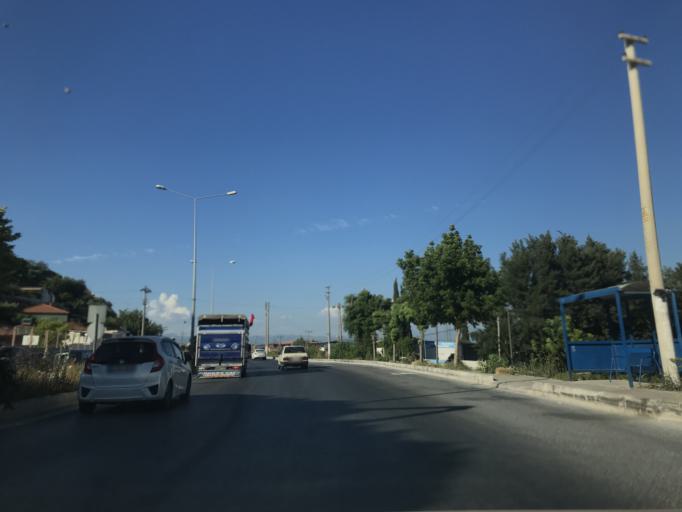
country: TR
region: Aydin
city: Soeke
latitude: 37.7840
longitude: 27.4634
